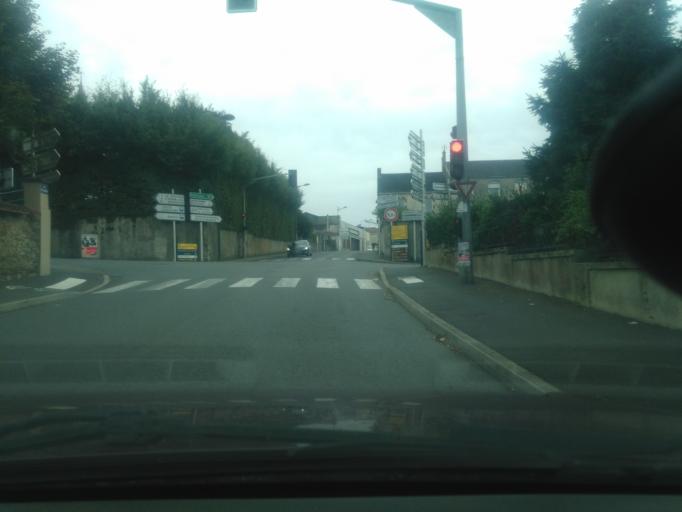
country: FR
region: Pays de la Loire
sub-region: Departement de la Vendee
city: La Chataigneraie
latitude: 46.6515
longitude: -0.7428
